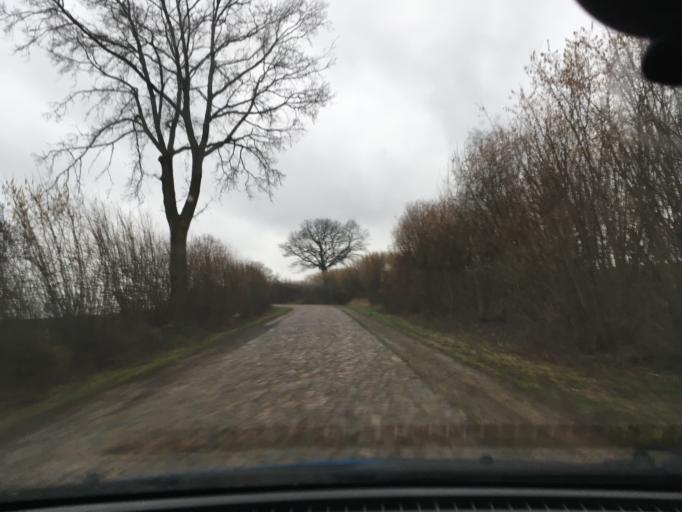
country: DE
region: Schleswig-Holstein
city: Schnakenbek
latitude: 53.3991
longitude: 10.5106
